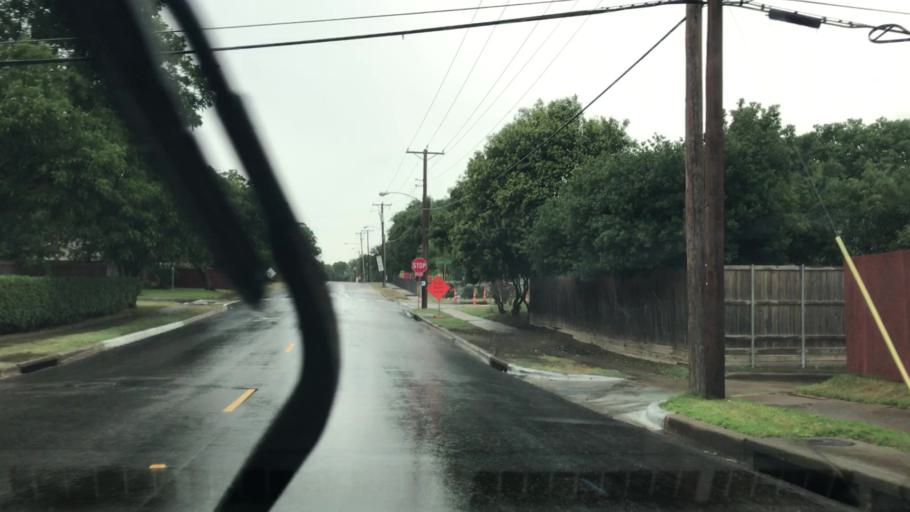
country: US
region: Texas
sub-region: Dallas County
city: Richardson
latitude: 32.9315
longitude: -96.7752
